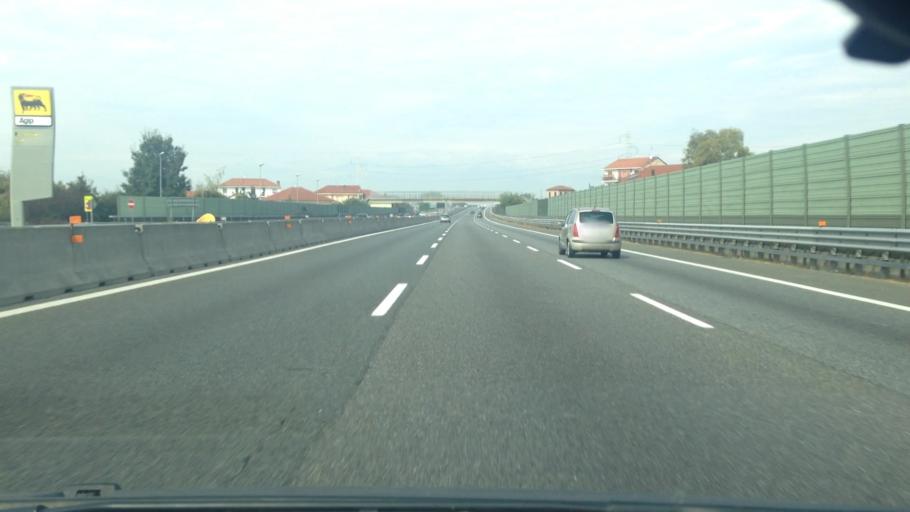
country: IT
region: Piedmont
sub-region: Provincia di Torino
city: Nichelino
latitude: 44.9820
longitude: 7.6451
